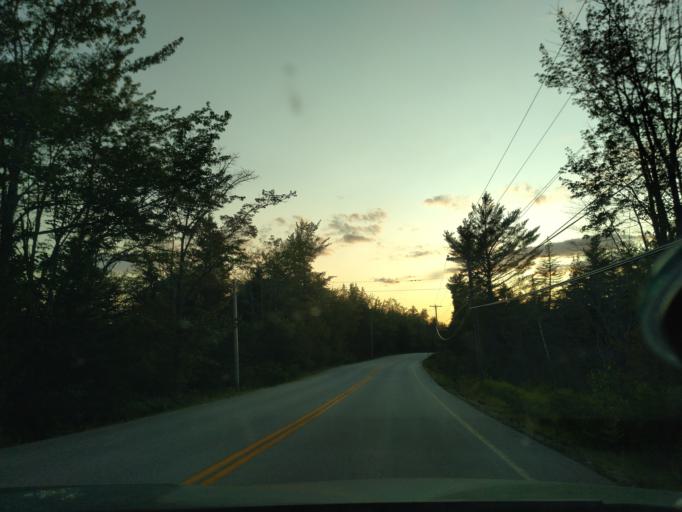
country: US
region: Maine
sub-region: Hancock County
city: Gouldsboro
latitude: 44.3933
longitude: -68.0620
